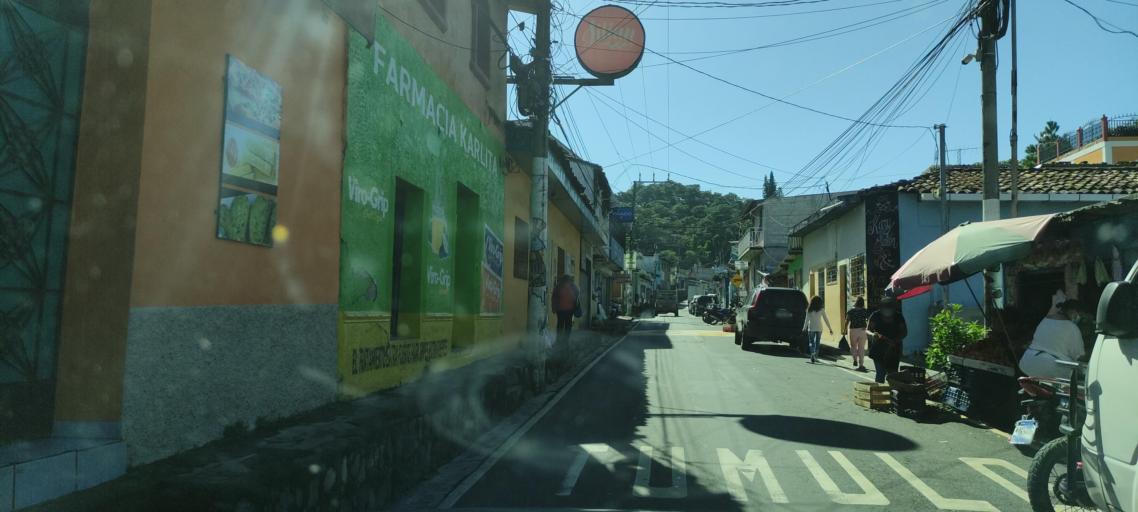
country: HN
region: Ocotepeque
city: Antigua Ocotepeque
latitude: 14.3169
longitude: -89.1710
